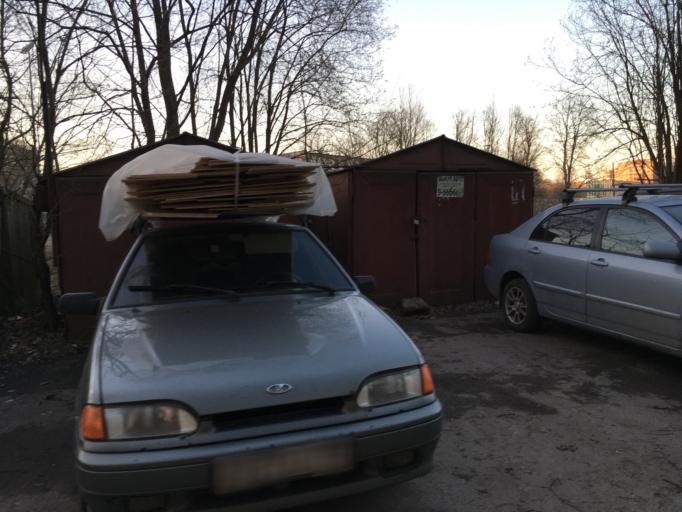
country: RU
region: Leningrad
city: Rybatskoye
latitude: 59.8948
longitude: 30.4816
